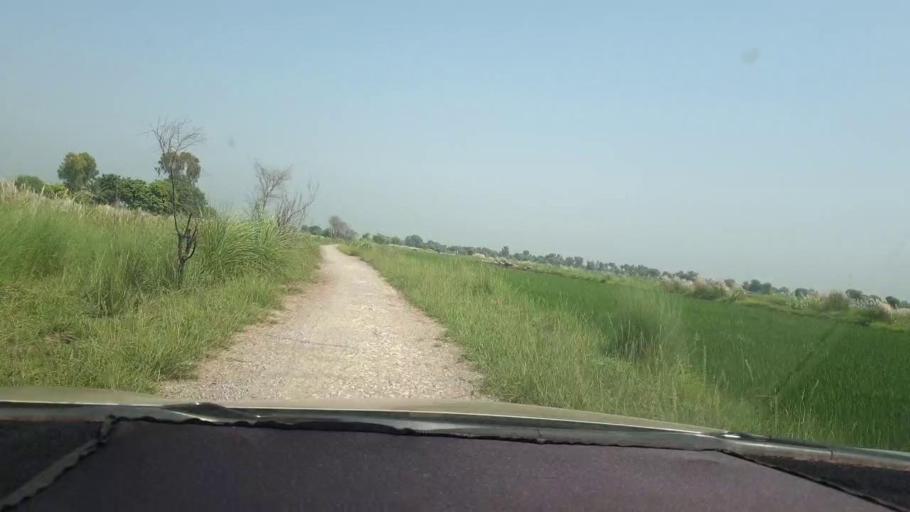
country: PK
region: Sindh
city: Kambar
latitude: 27.6023
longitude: 68.0637
